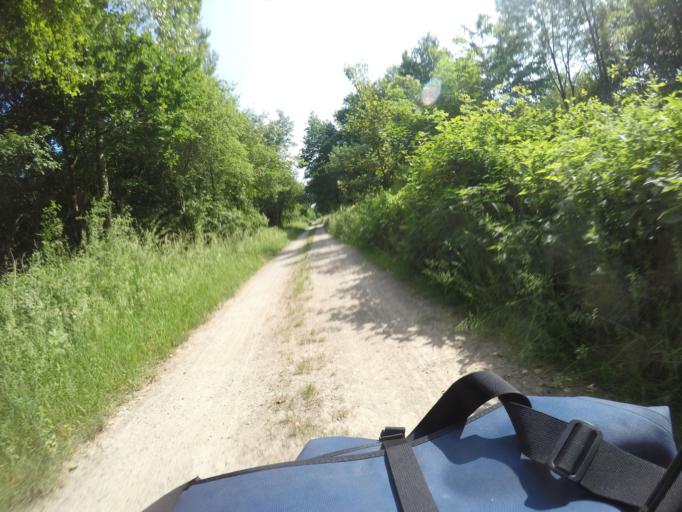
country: DE
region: Baden-Wuerttemberg
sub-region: Karlsruhe Region
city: Bietigheim
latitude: 48.9095
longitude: 8.2342
